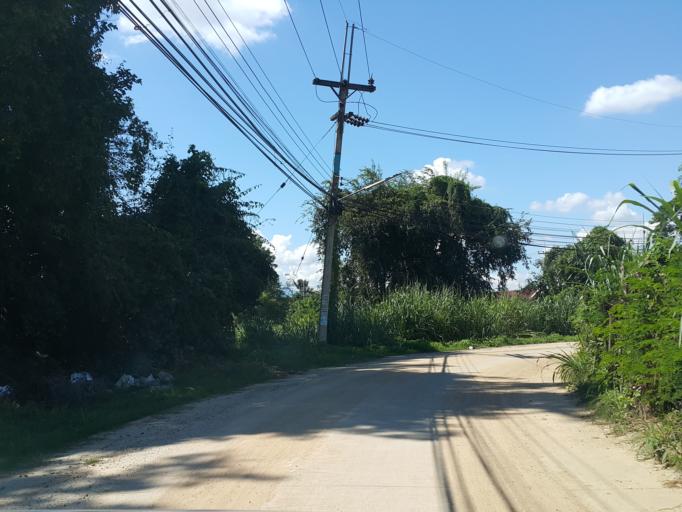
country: TH
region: Chiang Mai
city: San Sai
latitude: 18.8433
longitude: 99.0107
